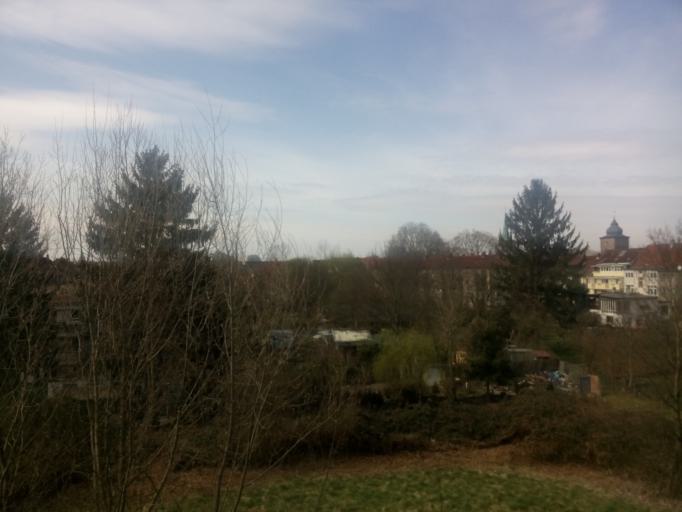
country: DE
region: Baden-Wuerttemberg
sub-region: Karlsruhe Region
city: Karlsruhe
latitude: 48.9955
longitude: 8.4720
